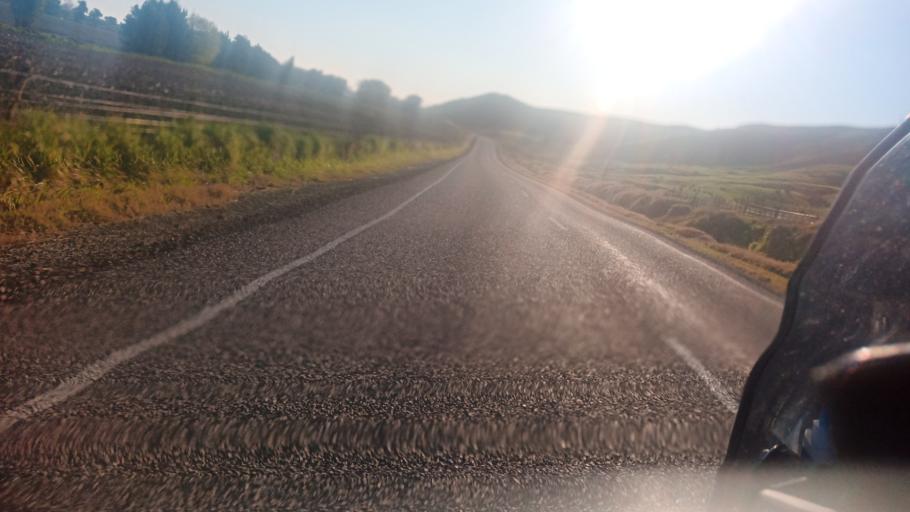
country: NZ
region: Hawke's Bay
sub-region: Wairoa District
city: Wairoa
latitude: -39.0477
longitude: 177.7696
